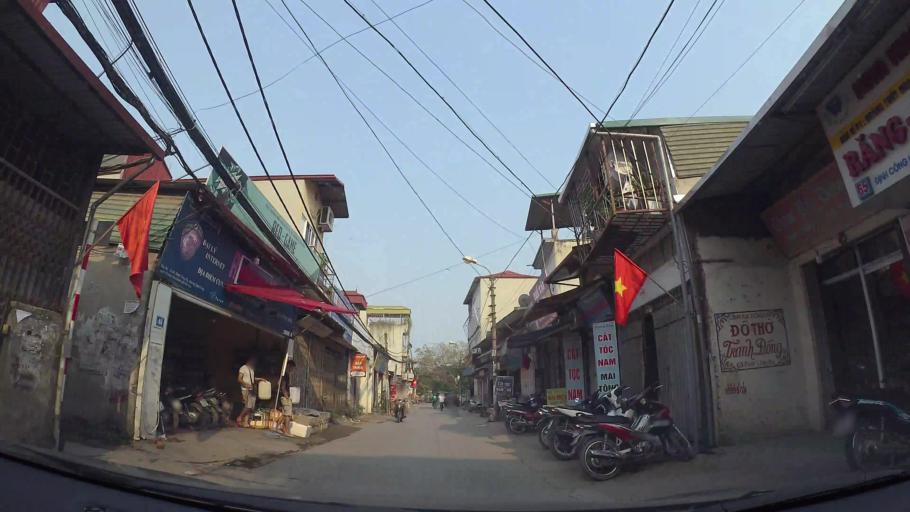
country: VN
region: Ha Noi
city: Thanh Xuan
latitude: 20.9822
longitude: 105.8290
